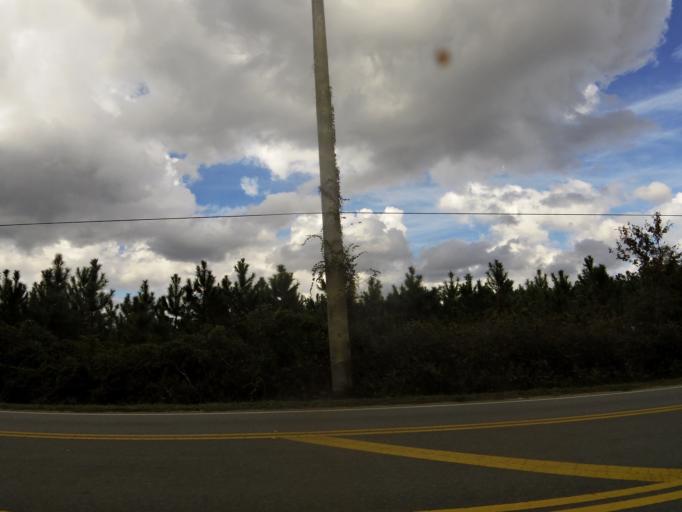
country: US
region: Florida
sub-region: Saint Johns County
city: Villano Beach
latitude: 30.0072
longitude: -81.4053
